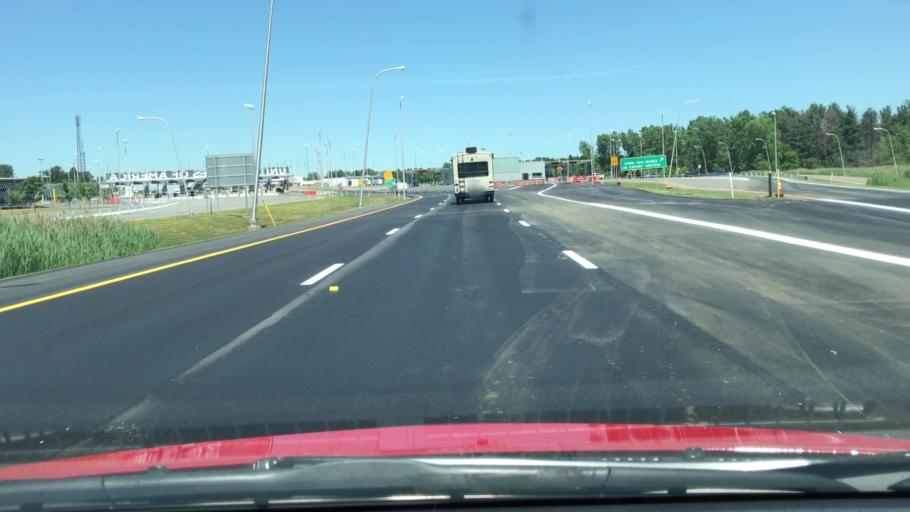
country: US
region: New York
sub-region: Clinton County
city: Champlain
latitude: 45.0037
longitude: -73.4527
